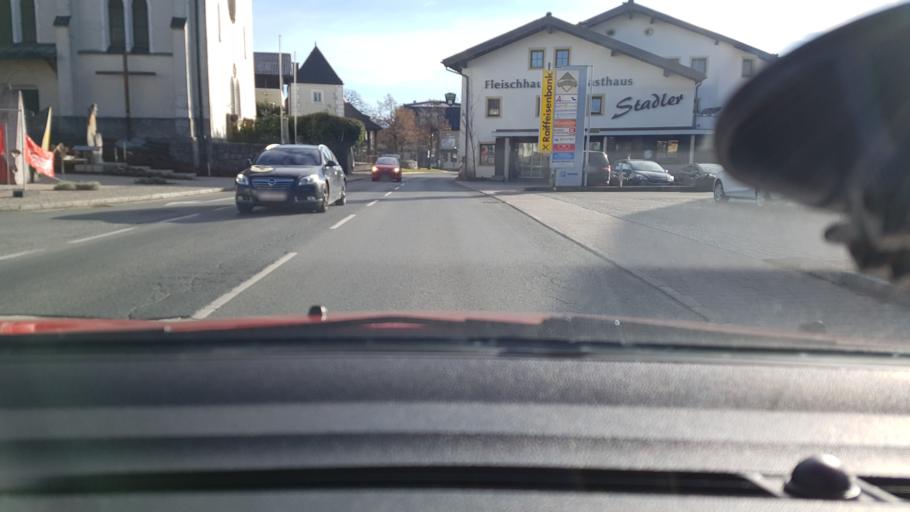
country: AT
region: Salzburg
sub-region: Politischer Bezirk Salzburg-Umgebung
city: Lamprechtshausen
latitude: 47.9924
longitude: 12.9563
